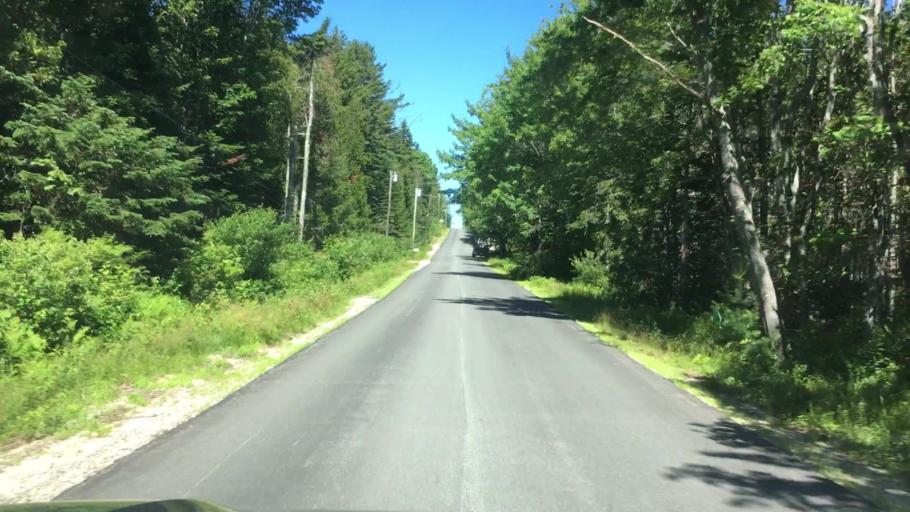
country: US
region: Maine
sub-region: Hancock County
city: Sedgwick
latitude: 44.3177
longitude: -68.6235
